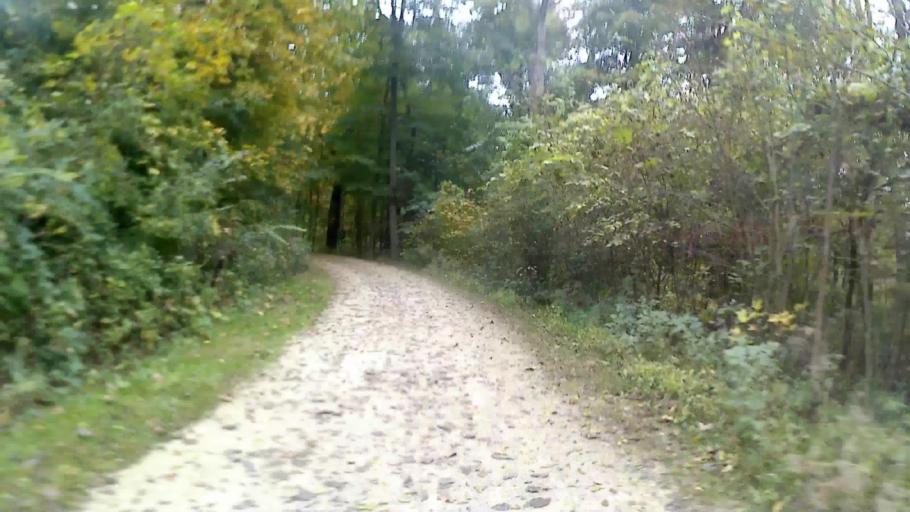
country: US
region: Illinois
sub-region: DuPage County
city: Warrenville
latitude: 41.8240
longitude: -88.1723
